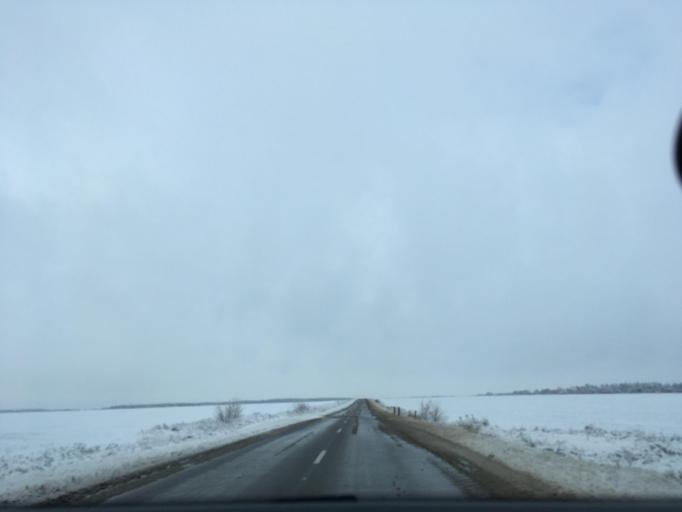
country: RU
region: Voronezj
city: Ol'khovatka
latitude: 50.1371
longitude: 39.2024
